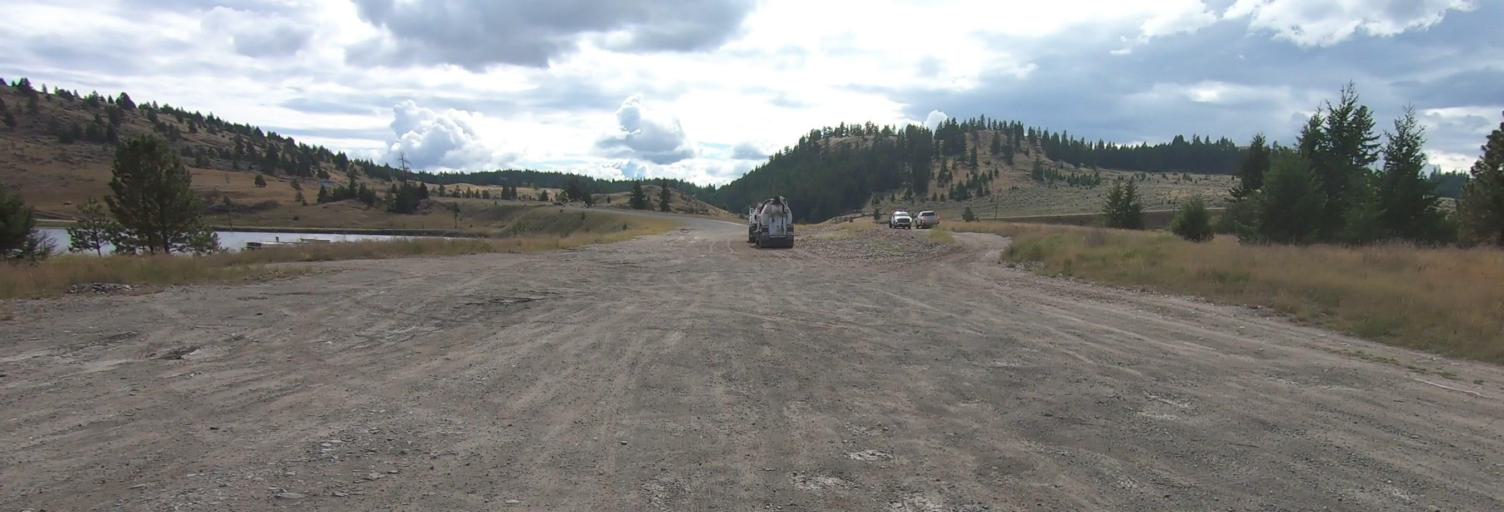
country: CA
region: British Columbia
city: Kamloops
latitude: 50.6184
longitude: -120.4474
